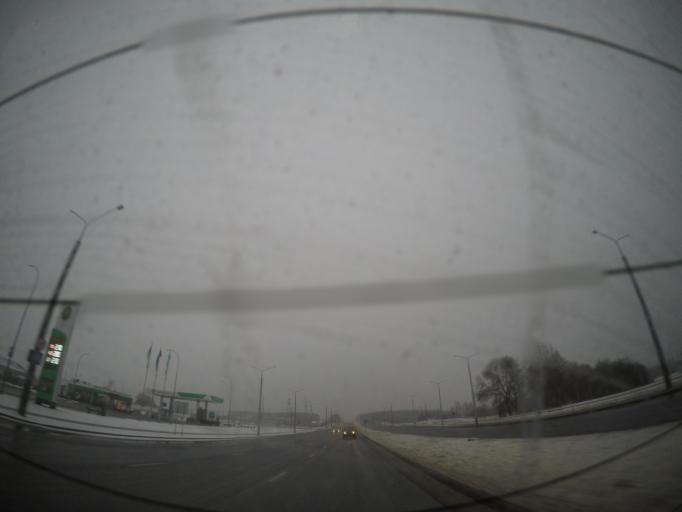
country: BY
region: Grodnenskaya
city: Hrodna
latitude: 53.6376
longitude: 23.8129
